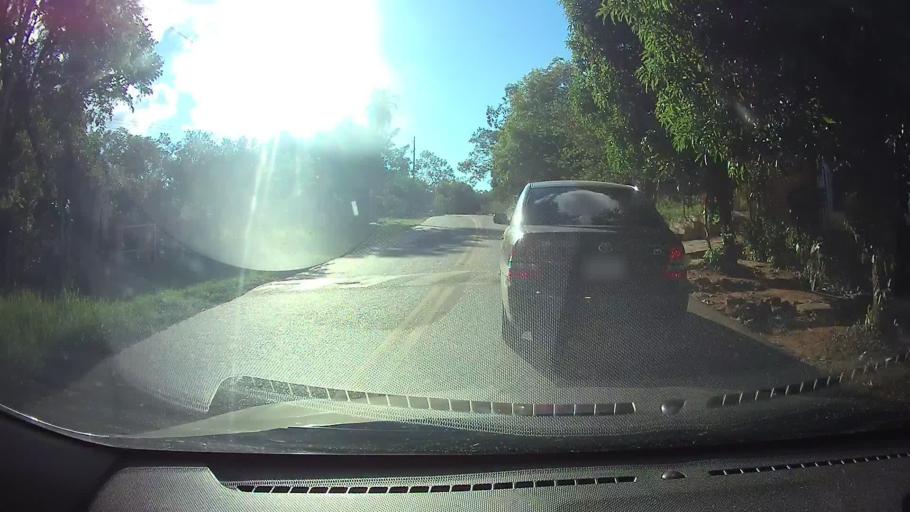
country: PY
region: Cordillera
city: Altos
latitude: -25.2765
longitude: -57.2309
